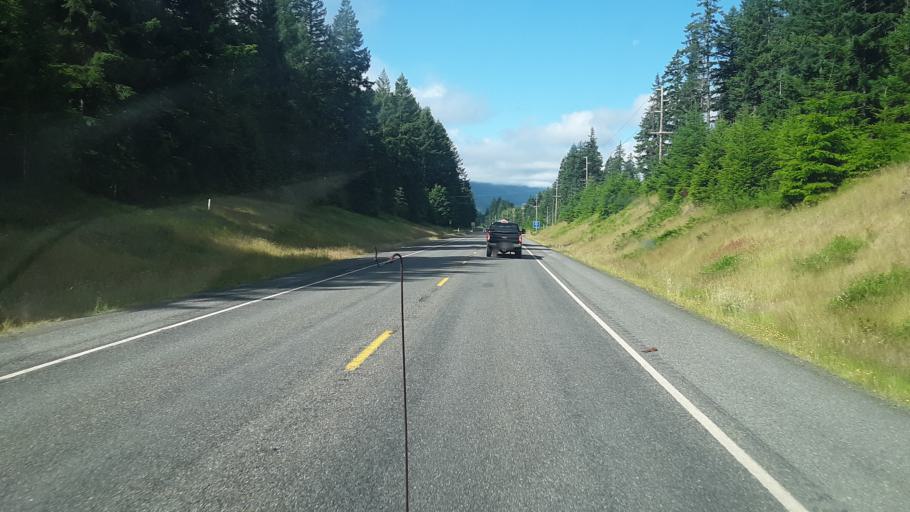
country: US
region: Washington
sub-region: Lewis County
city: Morton
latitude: 46.5539
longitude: -121.7332
